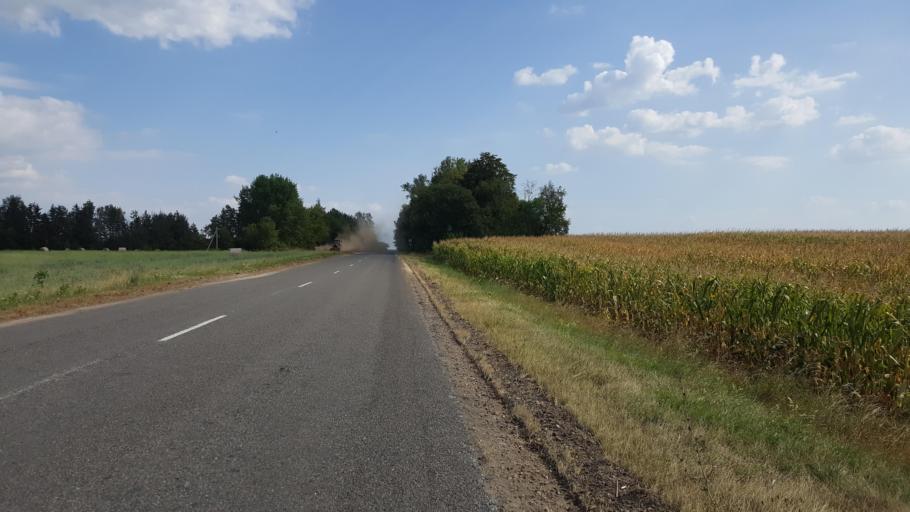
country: BY
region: Brest
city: Kamyanyets
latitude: 52.4150
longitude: 23.7844
